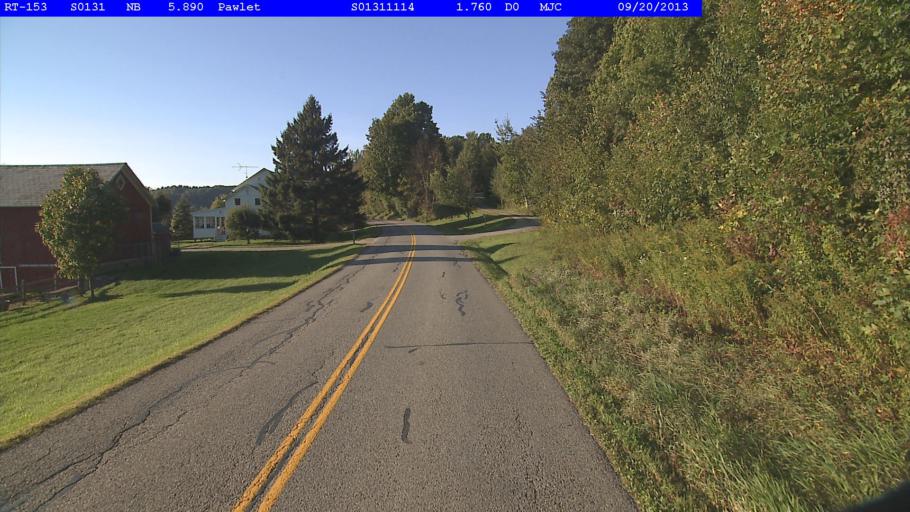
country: US
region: New York
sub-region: Washington County
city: Granville
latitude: 43.3393
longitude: -73.2435
